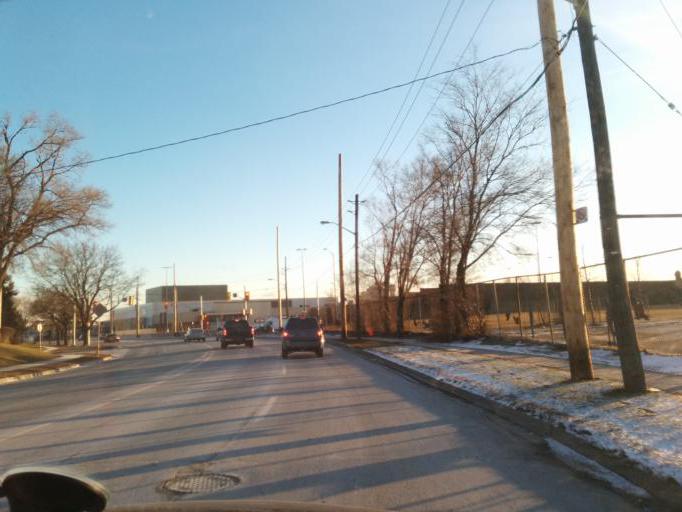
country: CA
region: Ontario
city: Etobicoke
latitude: 43.6350
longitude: -79.5567
